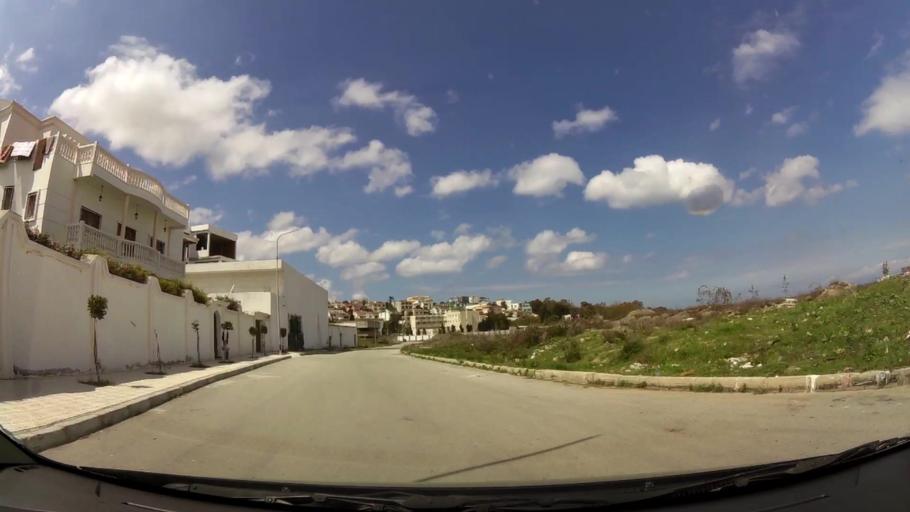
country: MA
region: Tanger-Tetouan
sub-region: Tanger-Assilah
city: Tangier
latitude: 35.7734
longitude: -5.7673
